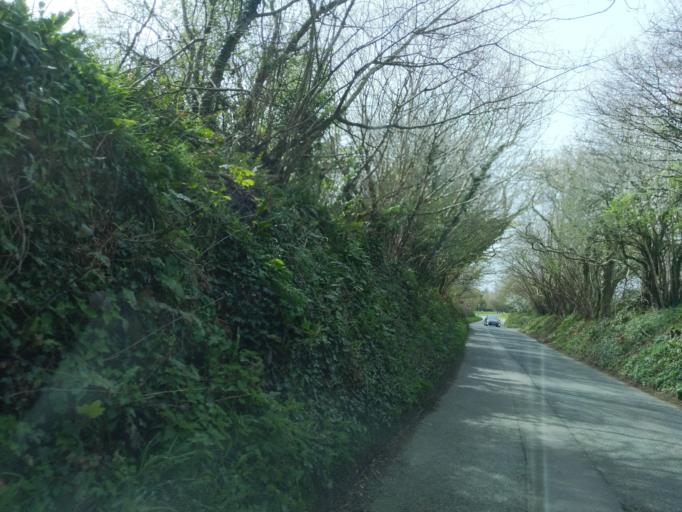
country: GB
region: England
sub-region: Devon
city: Yealmpton
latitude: 50.3912
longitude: -4.0094
